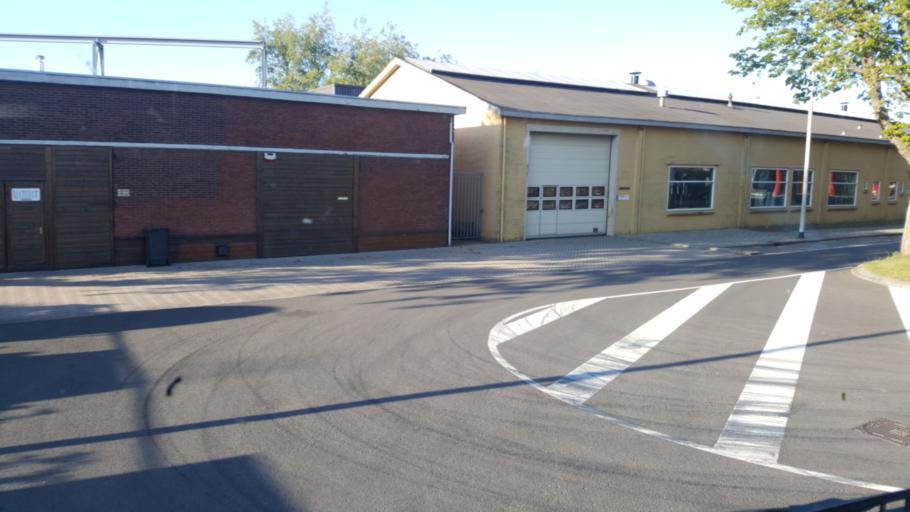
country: NL
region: South Holland
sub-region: Gemeente Zwijndrecht
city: Zwijndrecht
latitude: 51.8006
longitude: 4.6436
